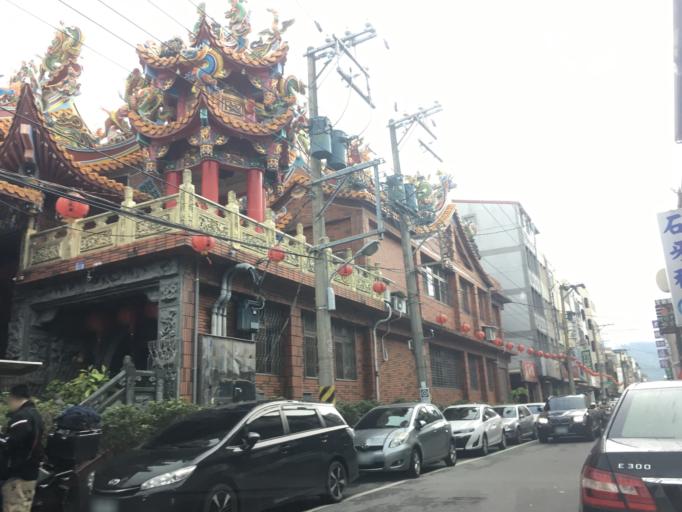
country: TW
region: Taiwan
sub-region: Hualien
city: Hualian
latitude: 23.9734
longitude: 121.6061
